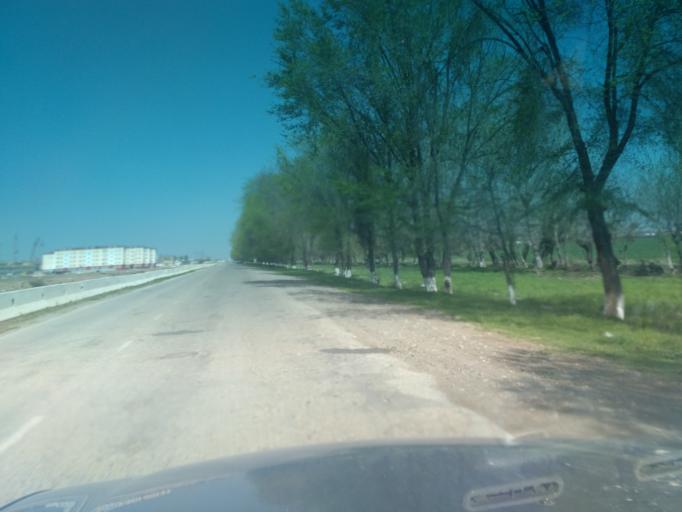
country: UZ
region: Sirdaryo
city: Guliston
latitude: 40.5084
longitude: 68.7960
